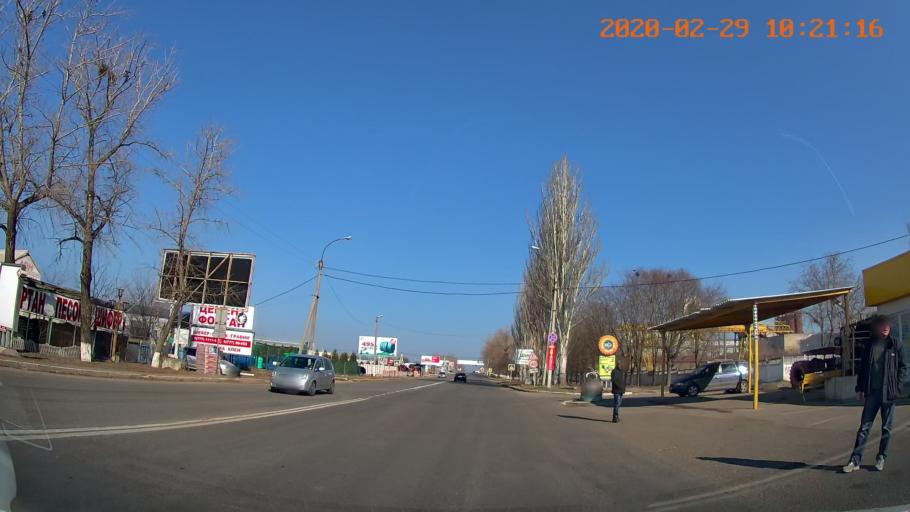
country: MD
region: Telenesti
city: Tiraspolul Nou
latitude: 46.8651
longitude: 29.6096
